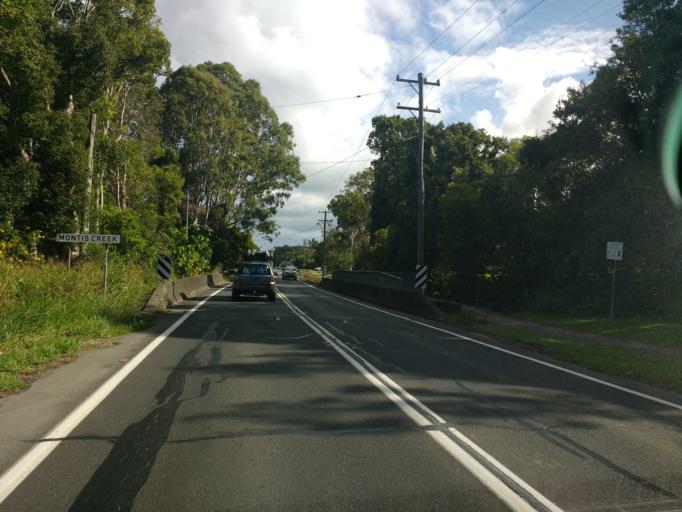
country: AU
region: New South Wales
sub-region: Richmond Valley
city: Evans Head
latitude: -29.0178
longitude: 153.4271
